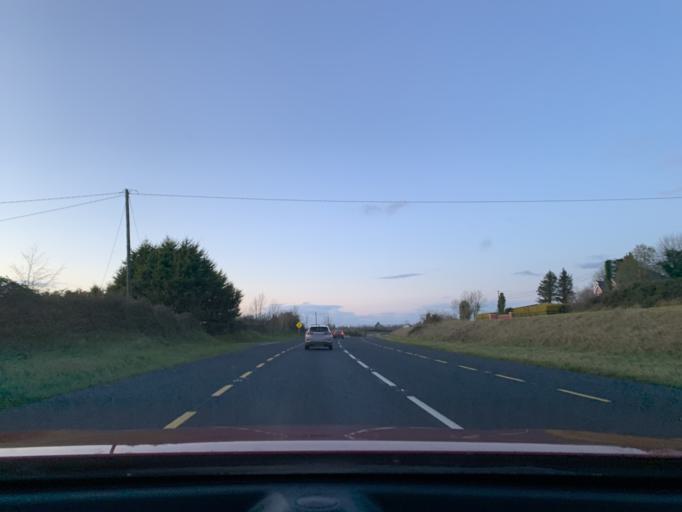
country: IE
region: Connaught
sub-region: County Leitrim
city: Carrick-on-Shannon
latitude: 53.8849
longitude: -7.9407
